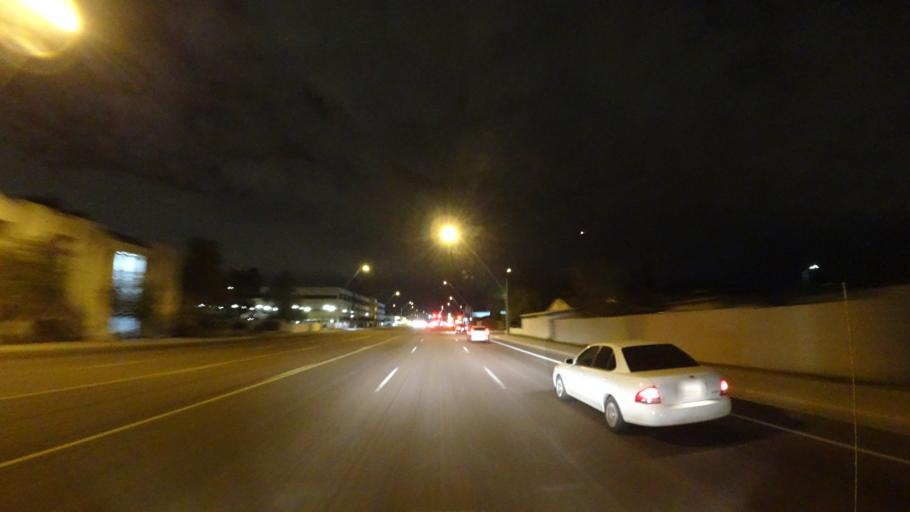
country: US
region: Arizona
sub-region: Maricopa County
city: Mesa
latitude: 33.4198
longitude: -111.8564
